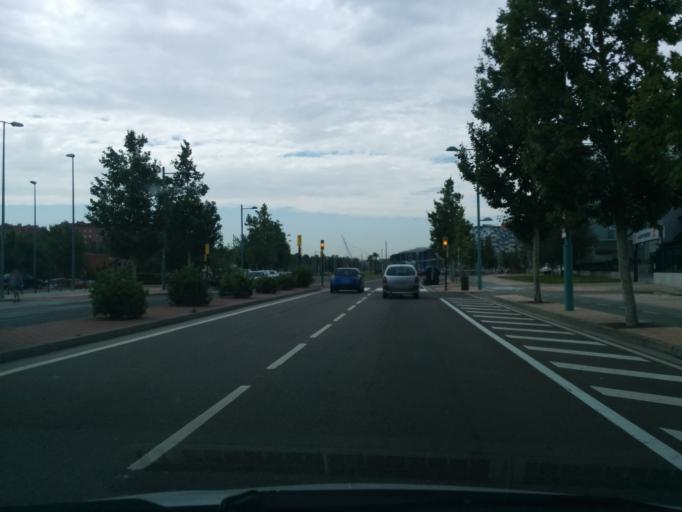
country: ES
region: Aragon
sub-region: Provincia de Zaragoza
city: Almozara
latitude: 41.6742
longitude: -0.8981
